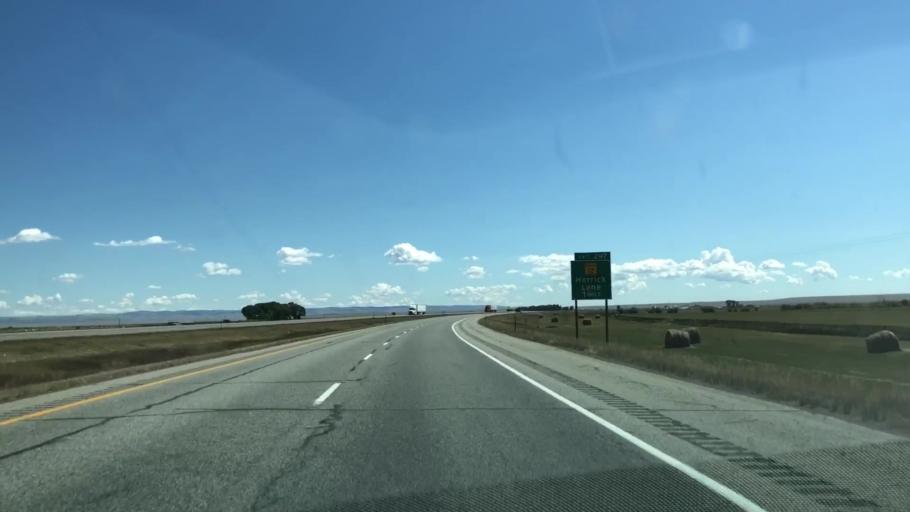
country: US
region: Wyoming
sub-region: Albany County
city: Laramie
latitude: 41.4108
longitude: -105.8388
